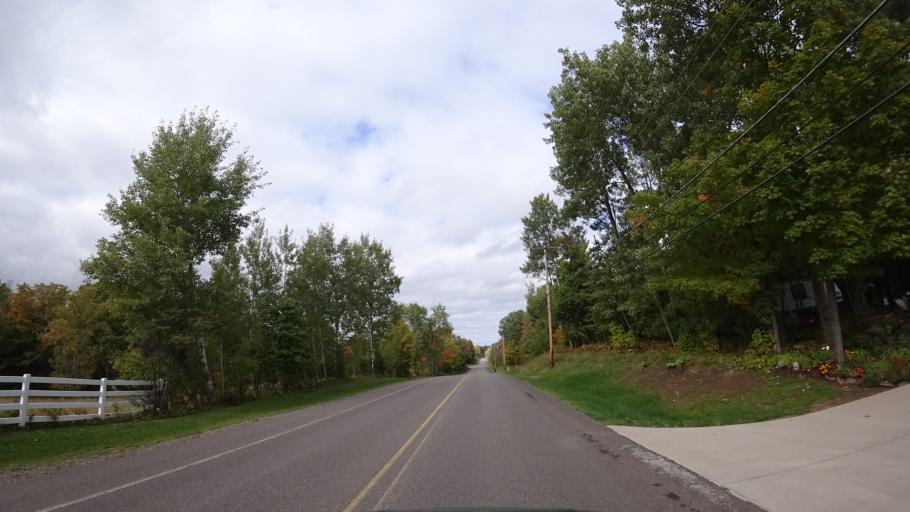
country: US
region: Michigan
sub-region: Marquette County
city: Trowbridge Park
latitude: 46.5408
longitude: -87.4374
